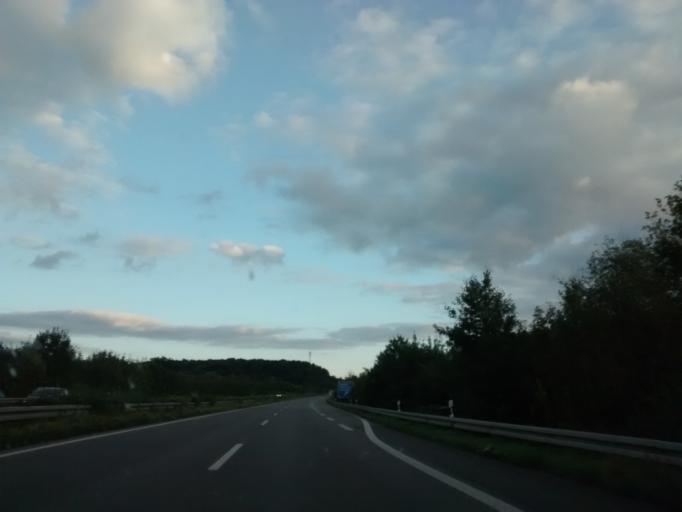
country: DE
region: Lower Saxony
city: Bissendorf
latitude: 52.2041
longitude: 8.1374
